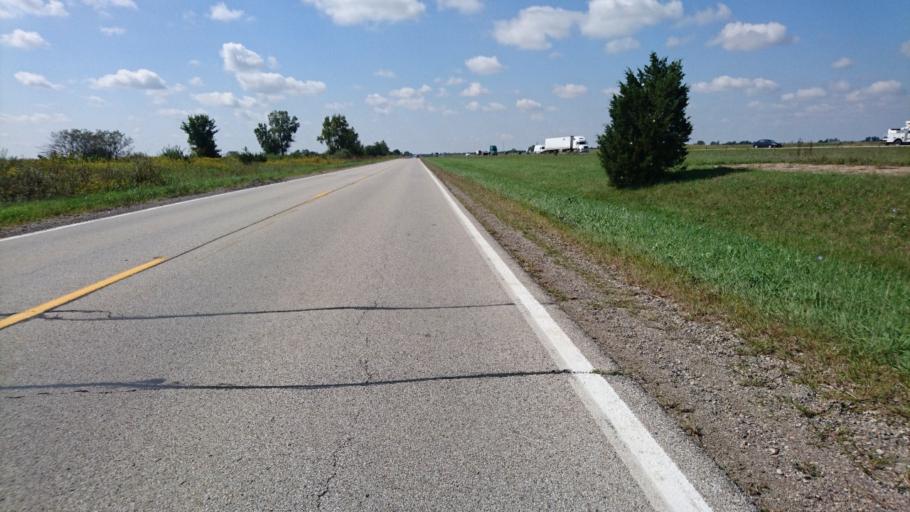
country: US
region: Illinois
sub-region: McLean County
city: Lexington
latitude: 40.6182
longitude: -88.8195
